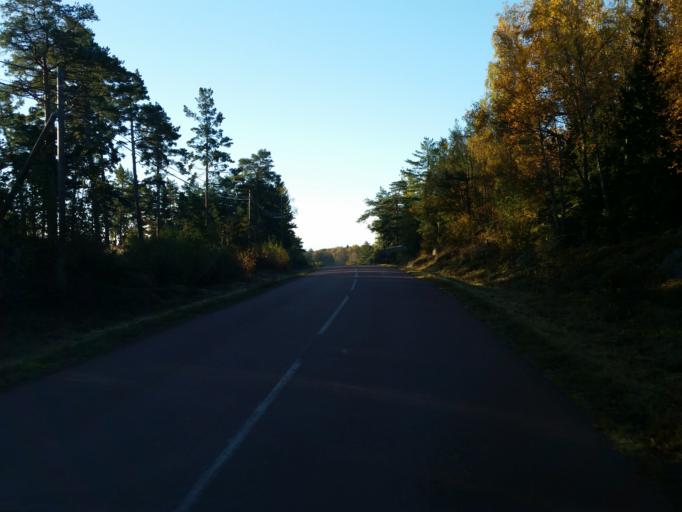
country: AX
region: Alands skaergard
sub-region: Vardoe
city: Vardoe
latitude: 60.2514
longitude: 20.3707
